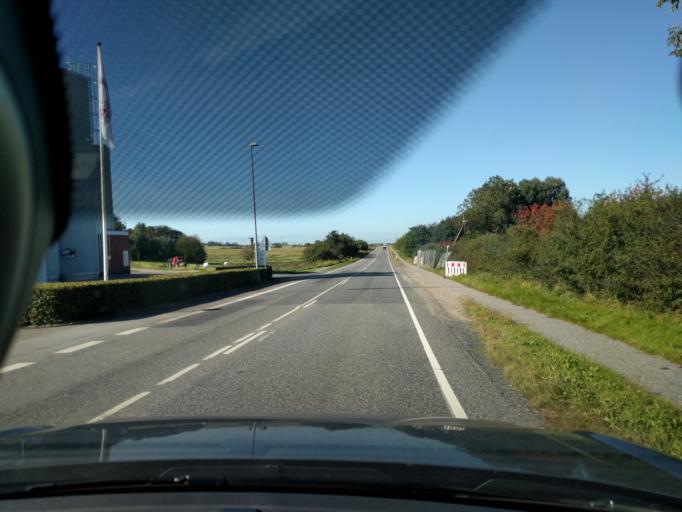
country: DK
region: North Denmark
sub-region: Vesthimmerland Kommune
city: Alestrup
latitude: 56.7106
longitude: 9.6226
